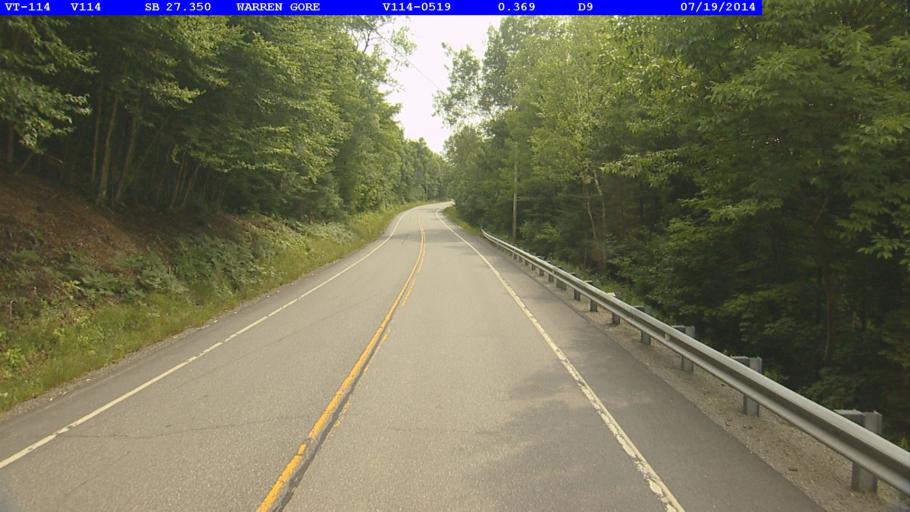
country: CA
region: Quebec
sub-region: Estrie
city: Coaticook
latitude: 44.8927
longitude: -71.8915
